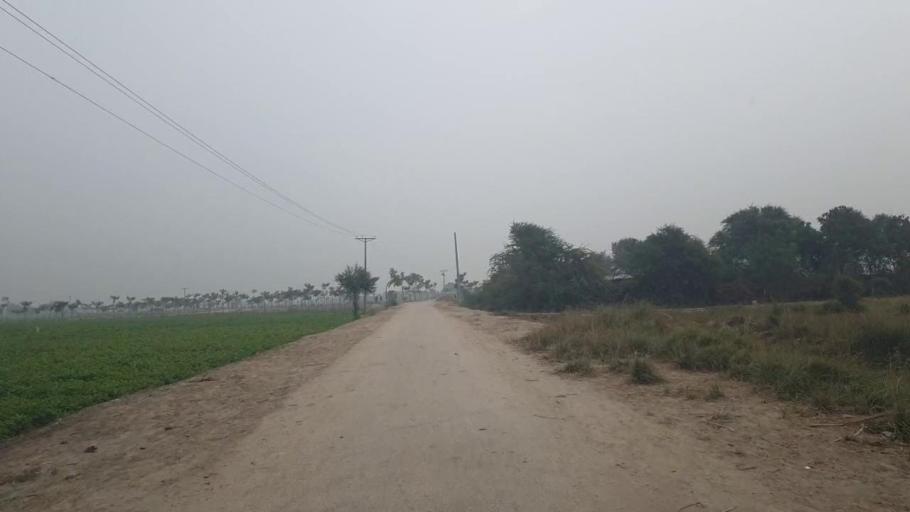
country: PK
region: Sindh
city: Tando Adam
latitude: 25.7479
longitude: 68.6733
